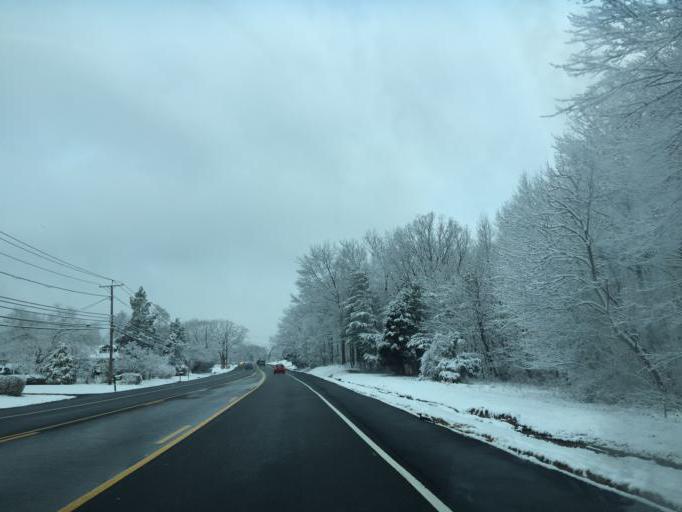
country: US
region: Maryland
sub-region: Harford County
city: Joppatowne
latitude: 39.4520
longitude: -76.3553
